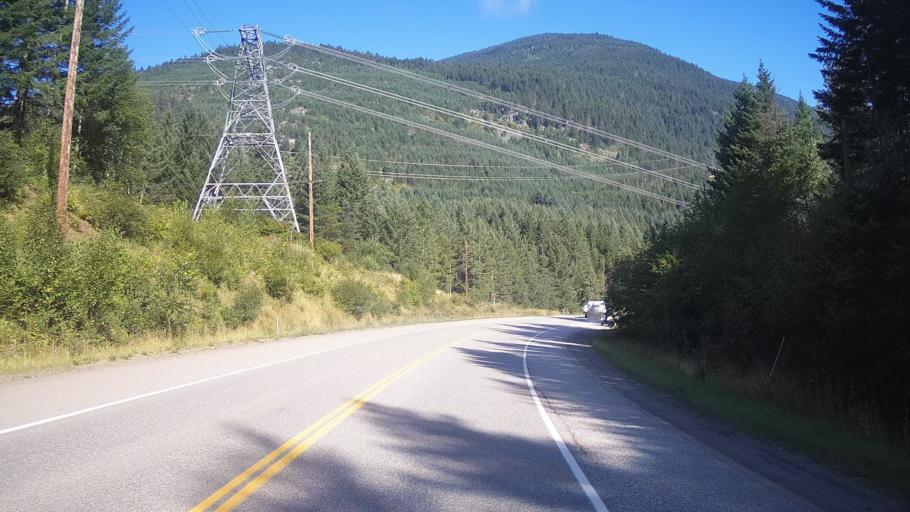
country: CA
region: British Columbia
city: Hope
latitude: 49.6633
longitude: -121.4174
